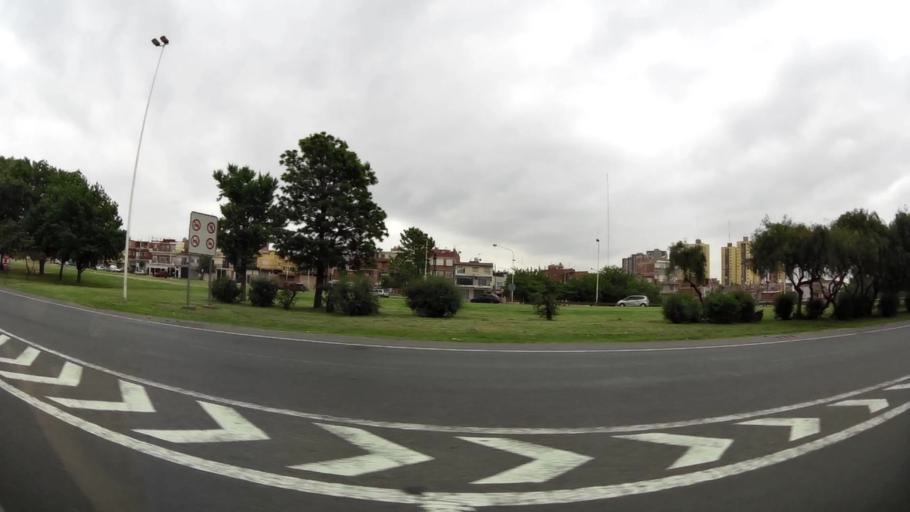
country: AR
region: Buenos Aires F.D.
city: Villa Lugano
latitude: -34.6895
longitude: -58.4876
